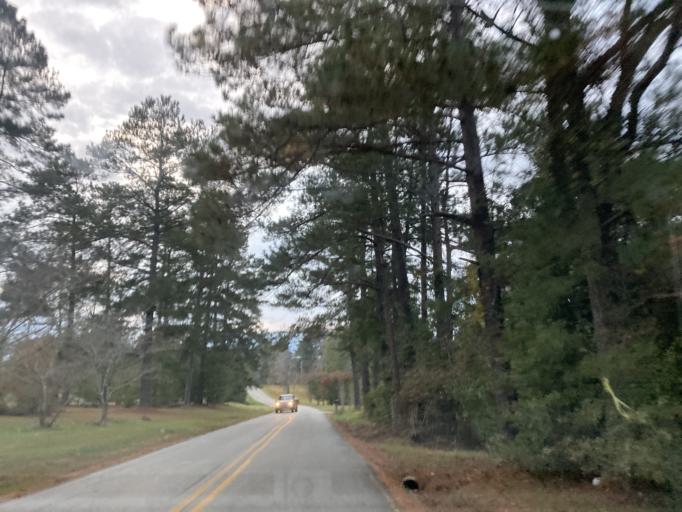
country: US
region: Georgia
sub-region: Jones County
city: Gray
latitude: 32.9776
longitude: -83.5188
